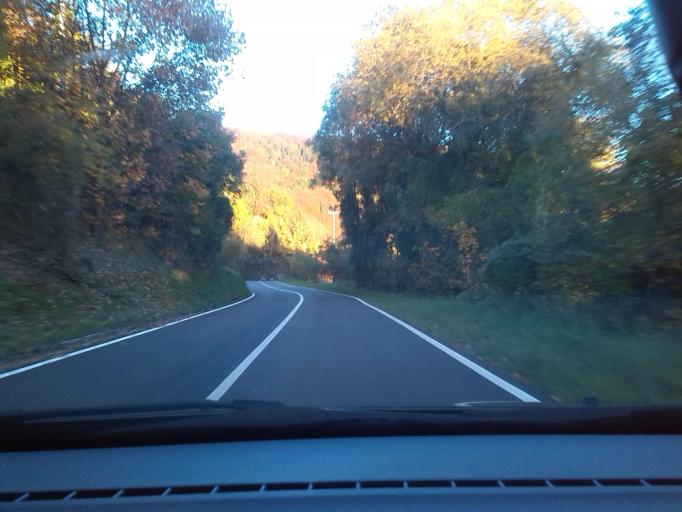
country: IT
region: Friuli Venezia Giulia
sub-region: Provincia di Udine
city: Savogna
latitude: 46.1924
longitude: 13.5378
